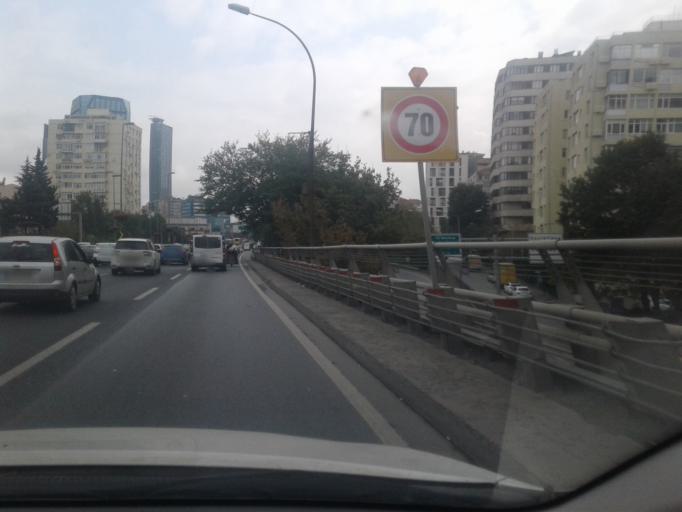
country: TR
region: Istanbul
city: Sisli
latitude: 41.0666
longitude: 29.0043
